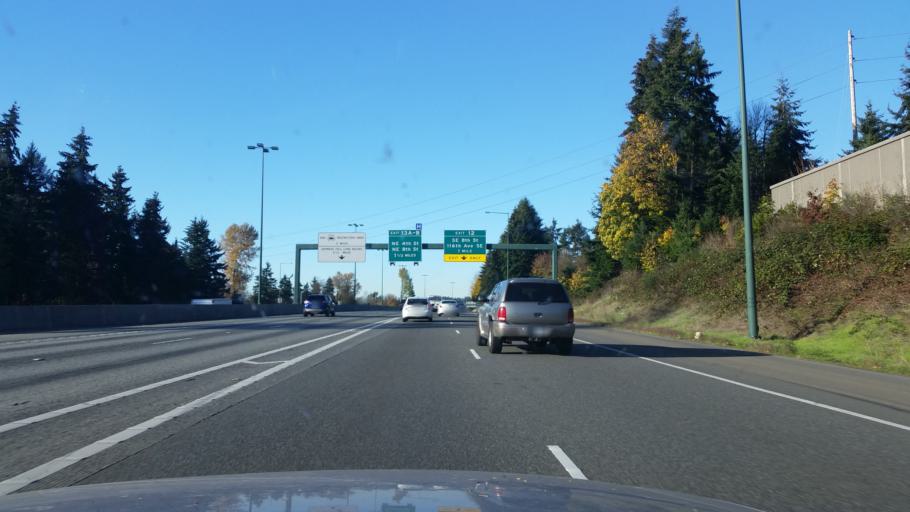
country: US
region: Washington
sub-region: King County
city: Newport
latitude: 47.5840
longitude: -122.1764
